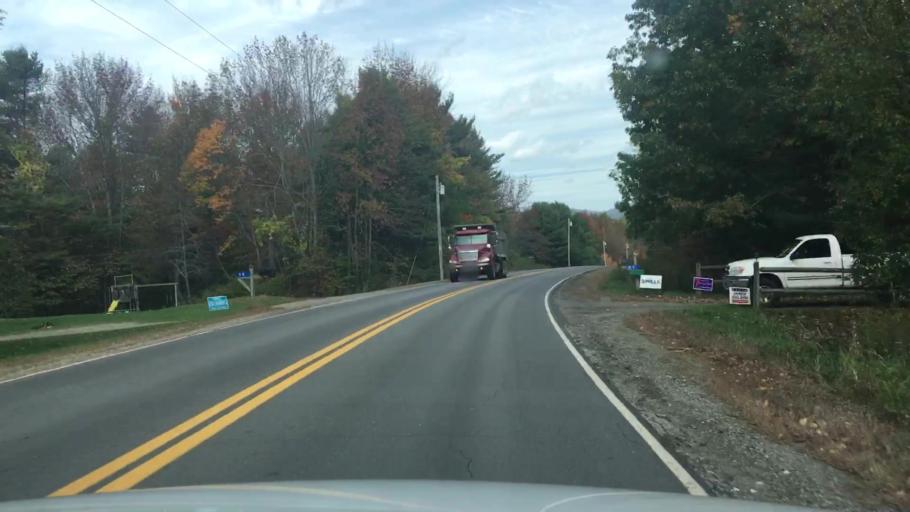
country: US
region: Maine
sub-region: Waldo County
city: Searsmont
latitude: 44.4004
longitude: -69.1366
